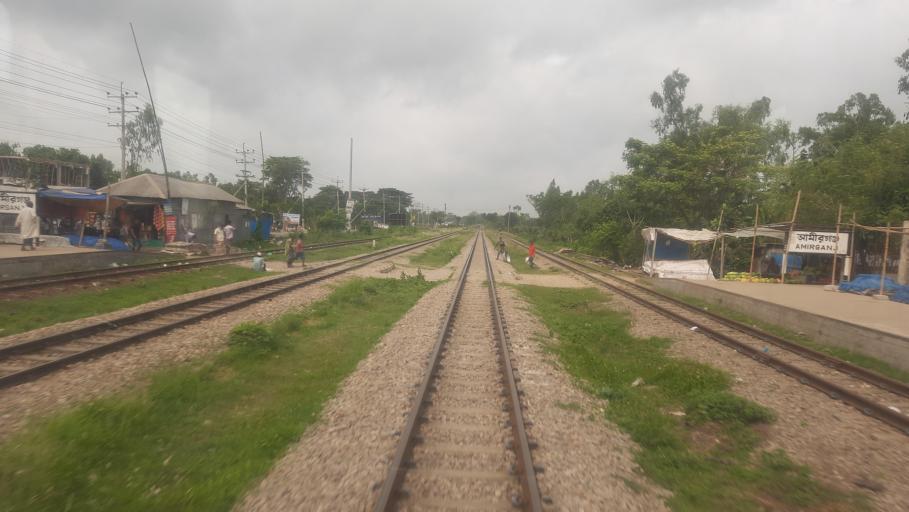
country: BD
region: Dhaka
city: Narsingdi
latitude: 23.9353
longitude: 90.7707
